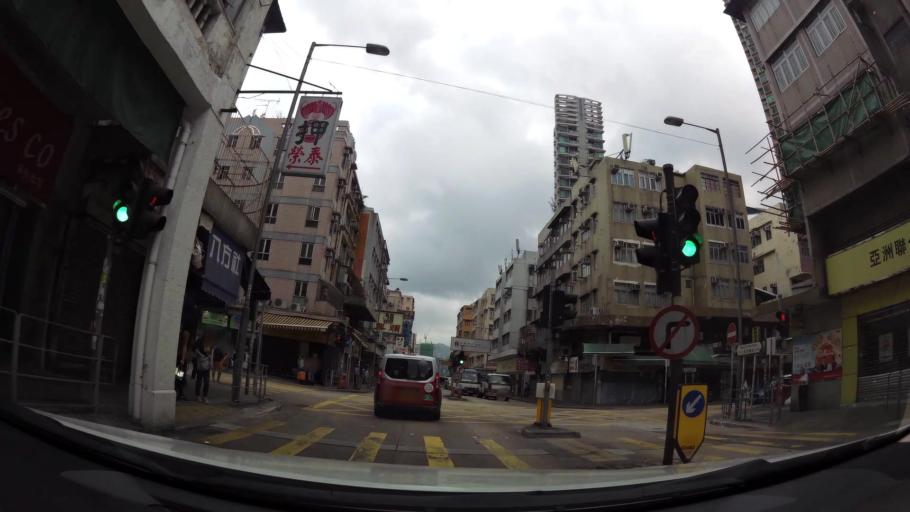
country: HK
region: Kowloon City
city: Kowloon
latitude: 22.3289
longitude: 114.1902
